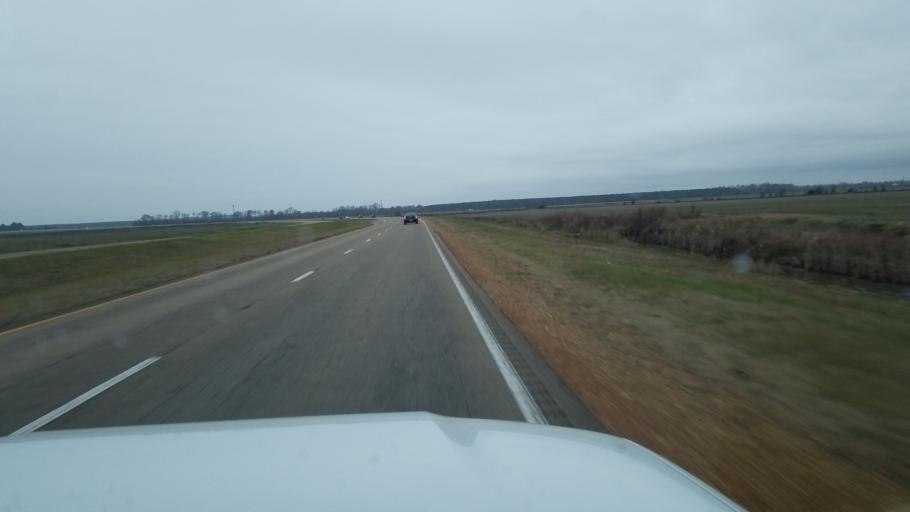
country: US
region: Mississippi
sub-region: Chickasaw County
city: Okolona
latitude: 33.9384
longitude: -88.7327
